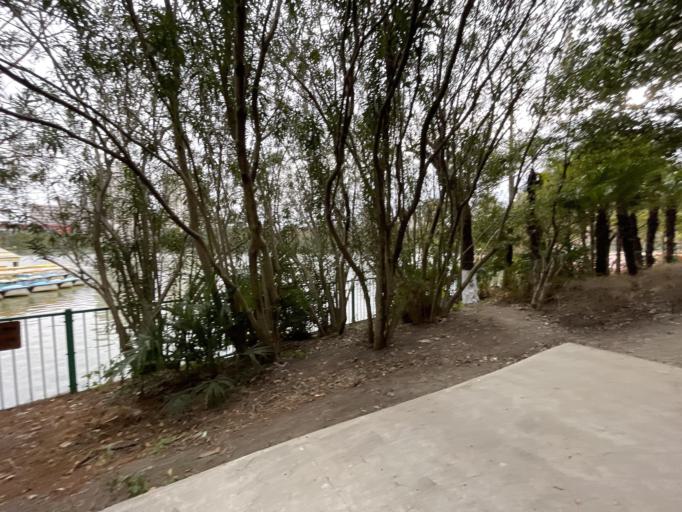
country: CN
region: Shanghai Shi
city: Yangpu
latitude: 31.2946
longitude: 121.5246
